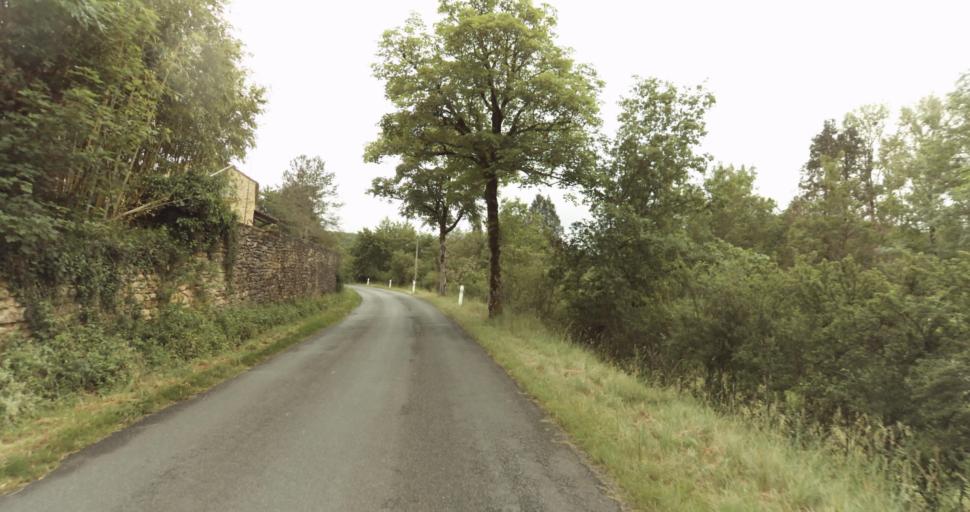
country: FR
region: Aquitaine
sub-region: Departement de la Dordogne
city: Beaumont-du-Perigord
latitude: 44.7647
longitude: 0.8047
